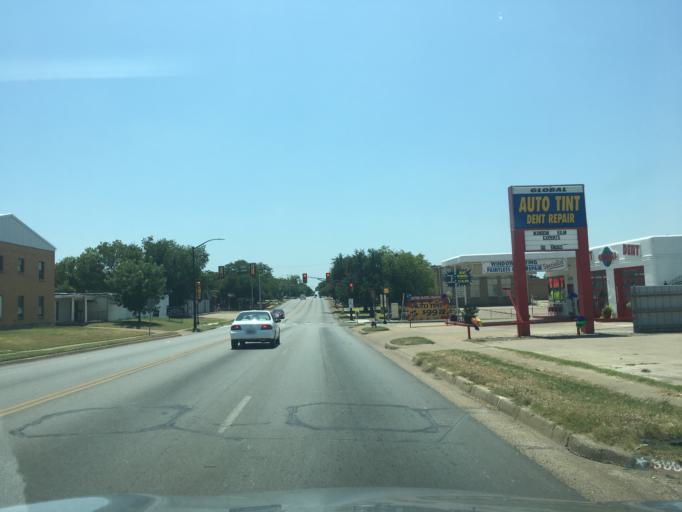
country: US
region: Texas
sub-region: Tarrant County
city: Edgecliff Village
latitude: 32.6929
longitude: -97.3530
